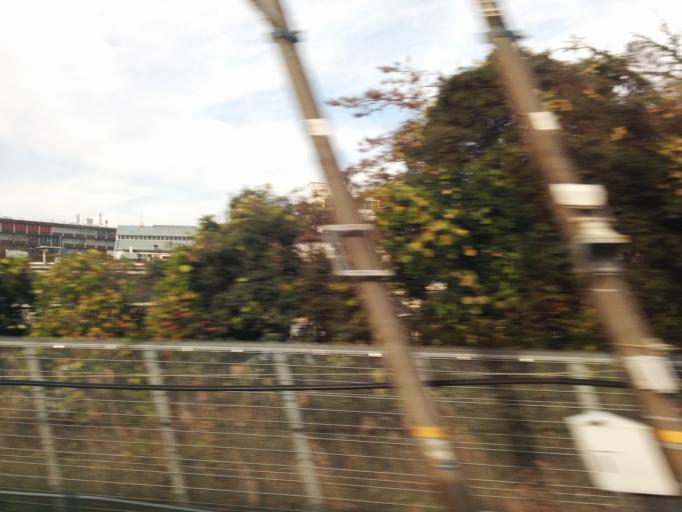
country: JP
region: Shiga Prefecture
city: Otsu-shi
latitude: 34.9728
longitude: 135.8878
